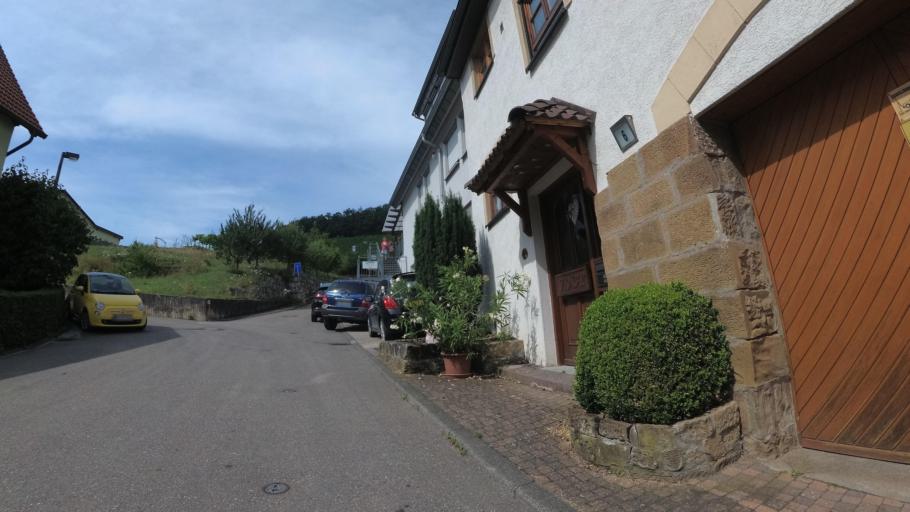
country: DE
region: Baden-Wuerttemberg
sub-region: Regierungsbezirk Stuttgart
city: Eberstadt
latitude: 49.1822
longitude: 9.2945
